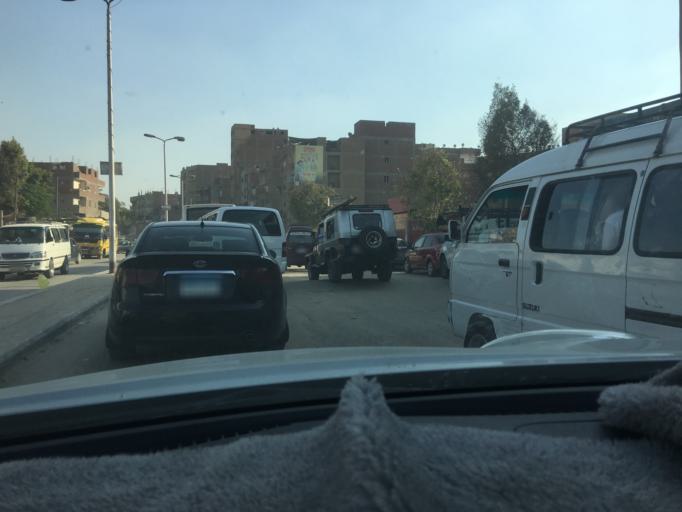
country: EG
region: Muhafazat al Qalyubiyah
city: Al Khankah
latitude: 30.1626
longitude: 31.3818
